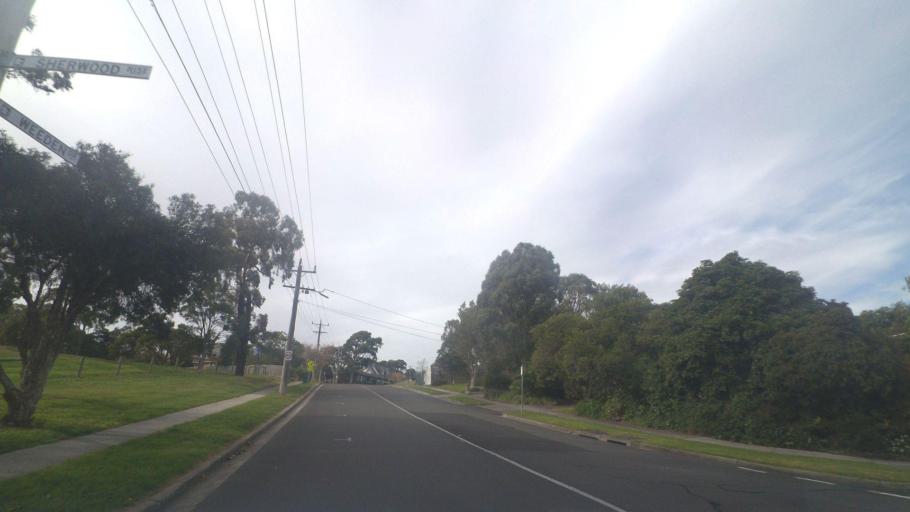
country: AU
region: Victoria
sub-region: Whitehorse
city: Vermont South
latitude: -37.8594
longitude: 145.1742
